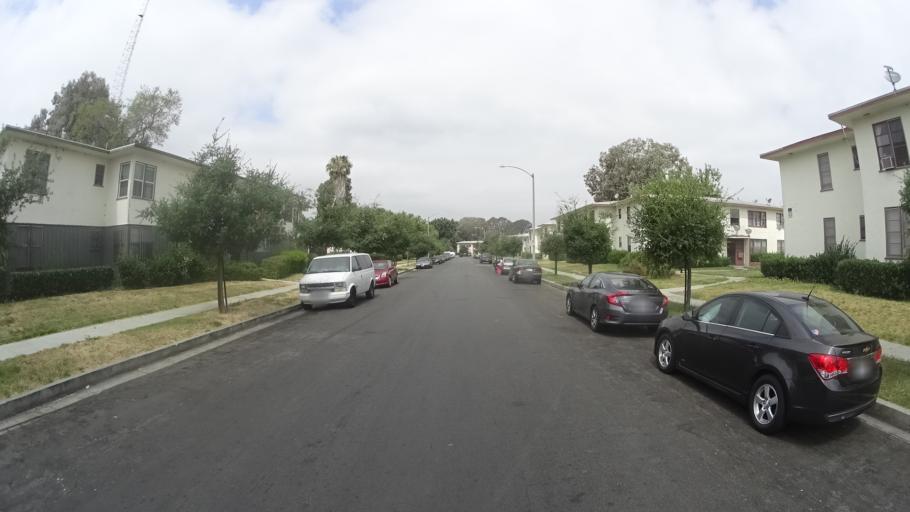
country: US
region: California
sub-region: Los Angeles County
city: View Park-Windsor Hills
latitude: 34.0203
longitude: -118.3465
